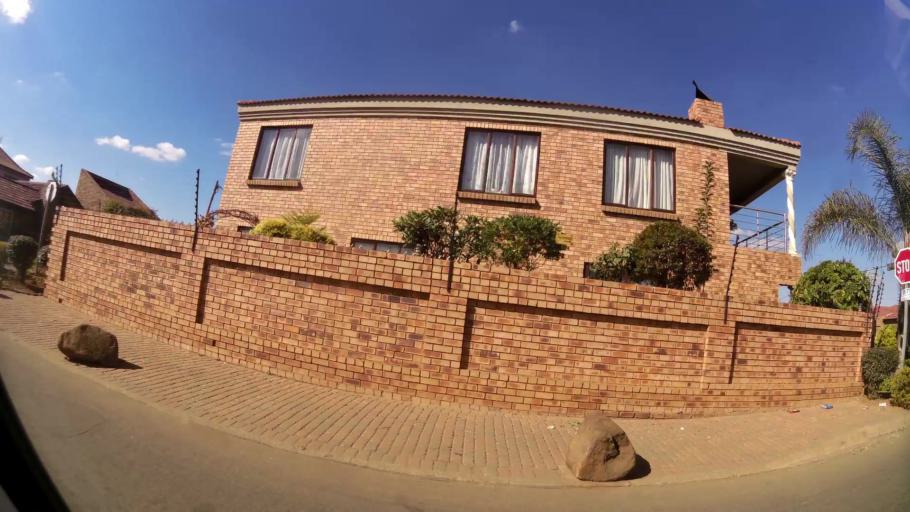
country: ZA
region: Gauteng
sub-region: City of Tshwane Metropolitan Municipality
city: Cullinan
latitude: -25.7173
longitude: 28.3999
